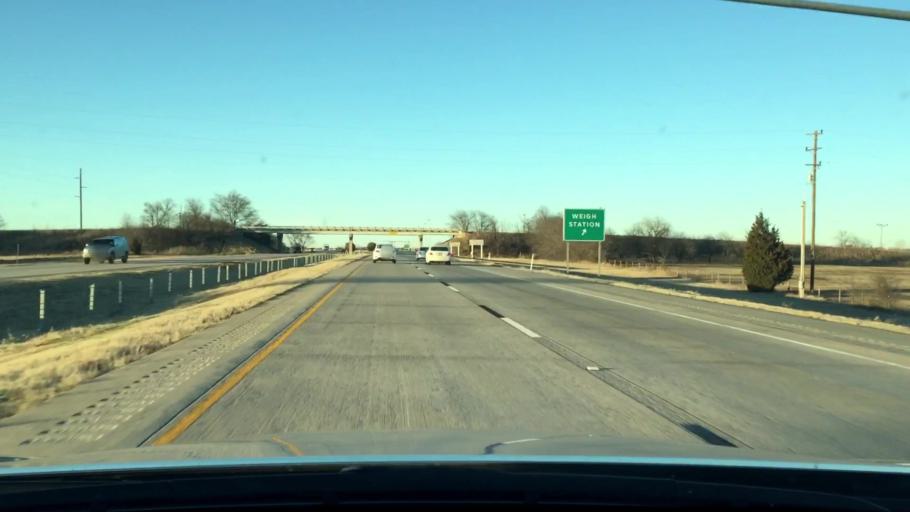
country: US
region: Oklahoma
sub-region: Love County
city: Marietta
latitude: 33.8951
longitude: -97.1343
